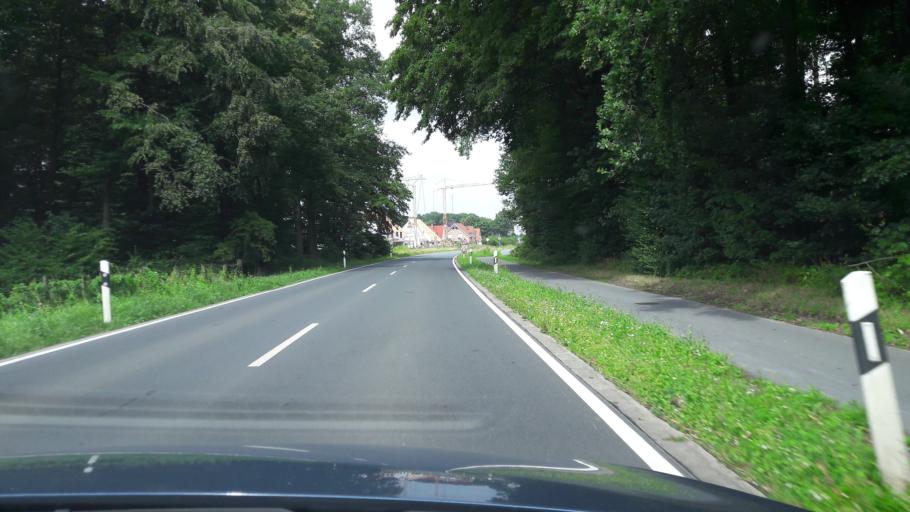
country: DE
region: North Rhine-Westphalia
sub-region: Regierungsbezirk Munster
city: Everswinkel
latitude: 51.9142
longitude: 7.8579
